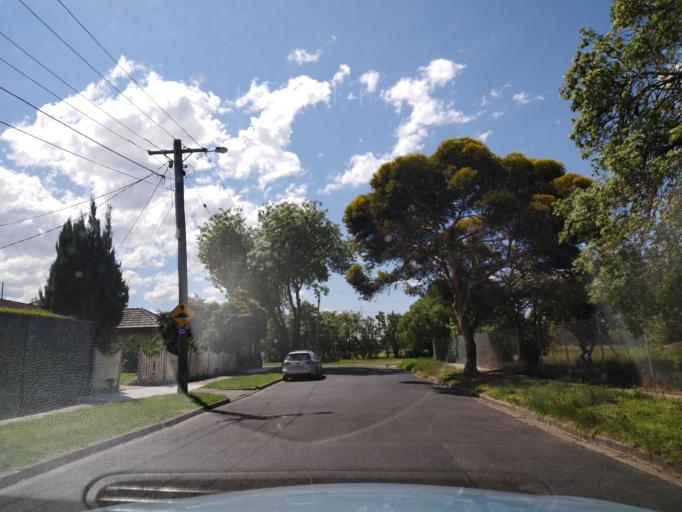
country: AU
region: Victoria
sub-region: Hobsons Bay
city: South Kingsville
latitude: -37.8306
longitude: 144.8747
